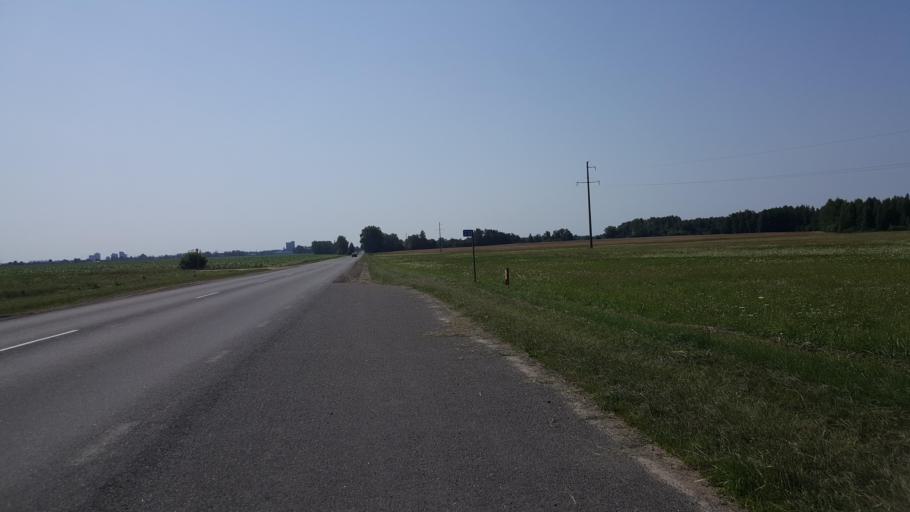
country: BY
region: Brest
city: Zhabinka
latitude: 52.2268
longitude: 23.9877
